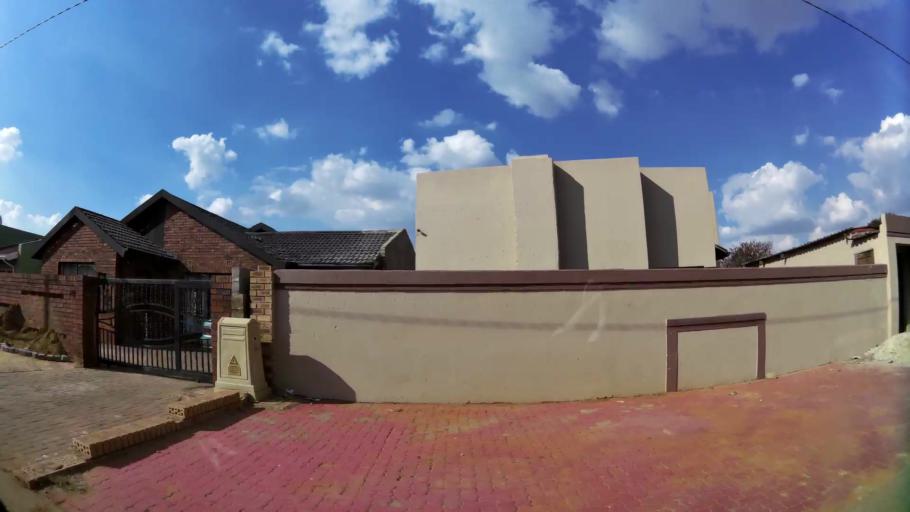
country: ZA
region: Gauteng
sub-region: City of Johannesburg Metropolitan Municipality
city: Soweto
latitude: -26.2233
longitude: 27.8618
